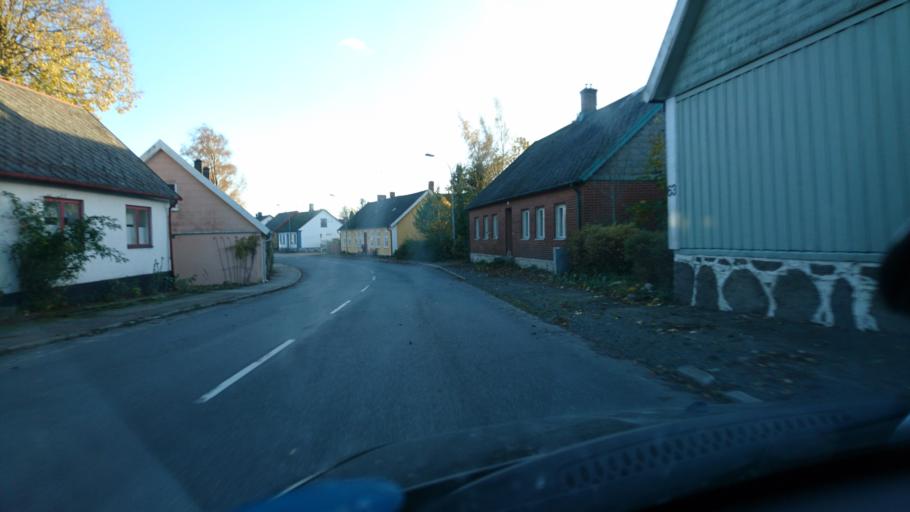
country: SE
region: Skane
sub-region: Tomelilla Kommun
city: Tomelilla
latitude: 55.5524
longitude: 14.1150
